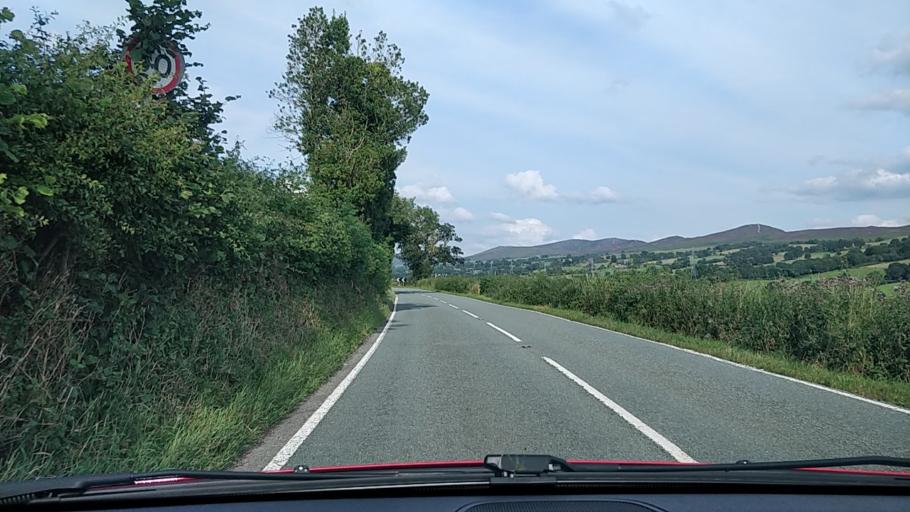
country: GB
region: Wales
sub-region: Denbighshire
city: Bryneglwys
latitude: 53.0073
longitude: -3.3133
